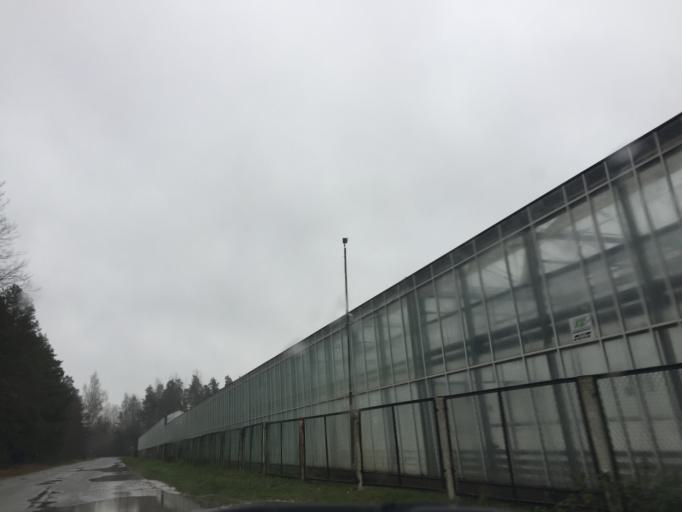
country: LV
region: Salas
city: Sala
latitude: 56.5002
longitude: 25.7760
